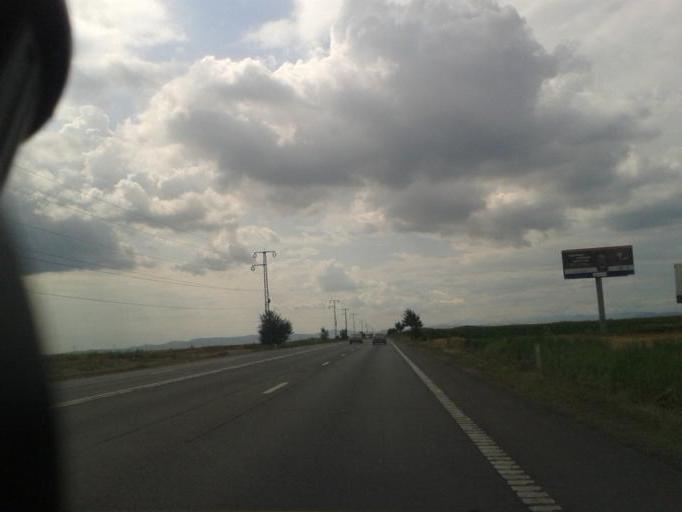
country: RO
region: Prahova
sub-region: Oras Baicoi
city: Tintea
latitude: 44.9909
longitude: 25.9113
